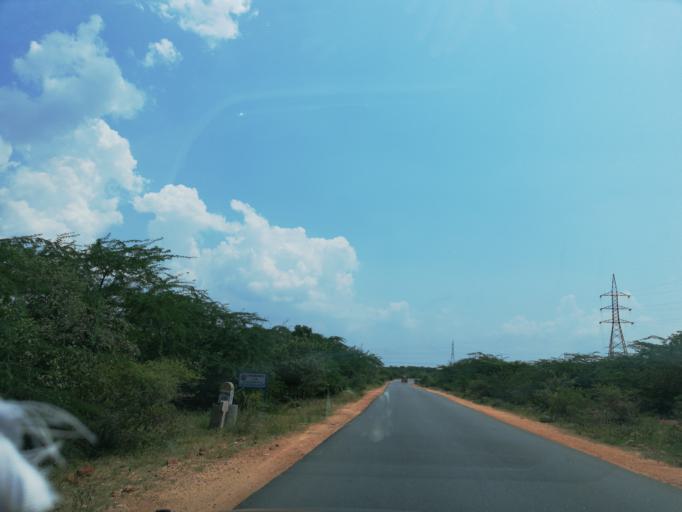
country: IN
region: Andhra Pradesh
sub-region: Guntur
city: Macherla
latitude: 16.5680
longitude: 79.3423
